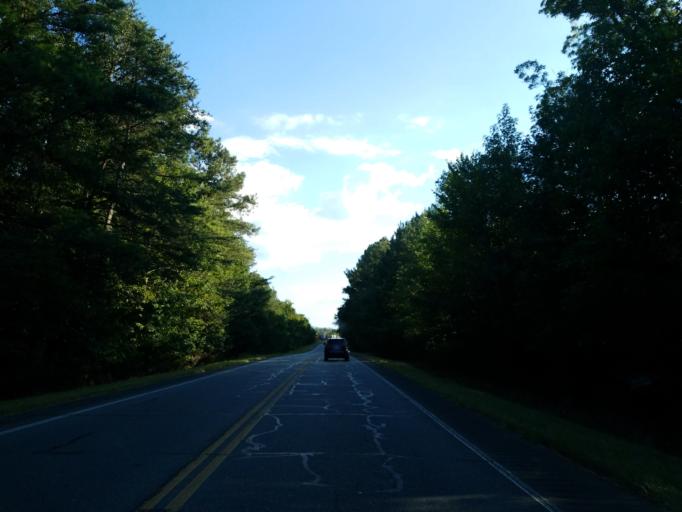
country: US
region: Georgia
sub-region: Murray County
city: Chatsworth
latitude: 34.9146
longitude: -84.7460
